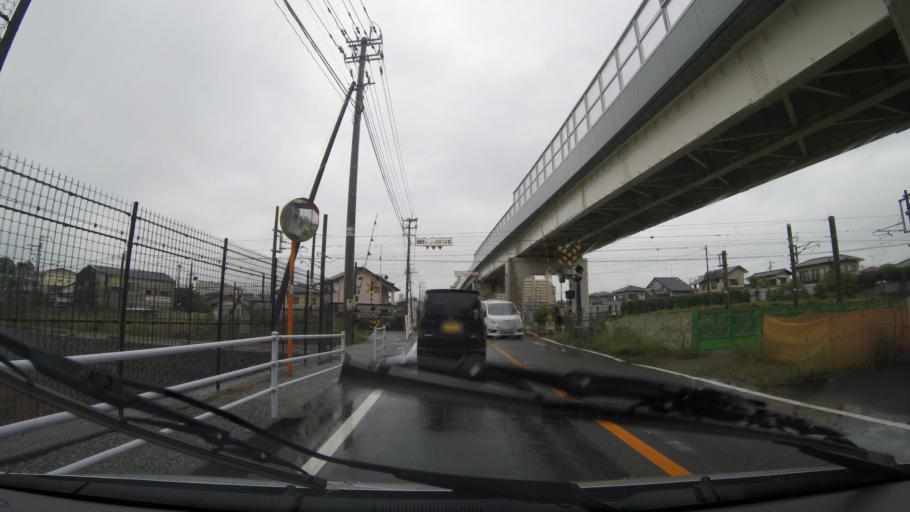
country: JP
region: Fukuoka
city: Koga
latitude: 33.7234
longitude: 130.4610
